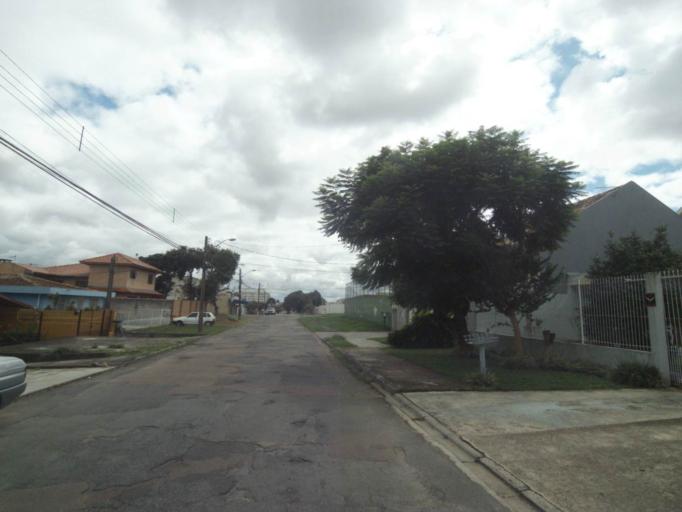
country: BR
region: Parana
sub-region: Curitiba
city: Curitiba
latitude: -25.4836
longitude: -49.2742
